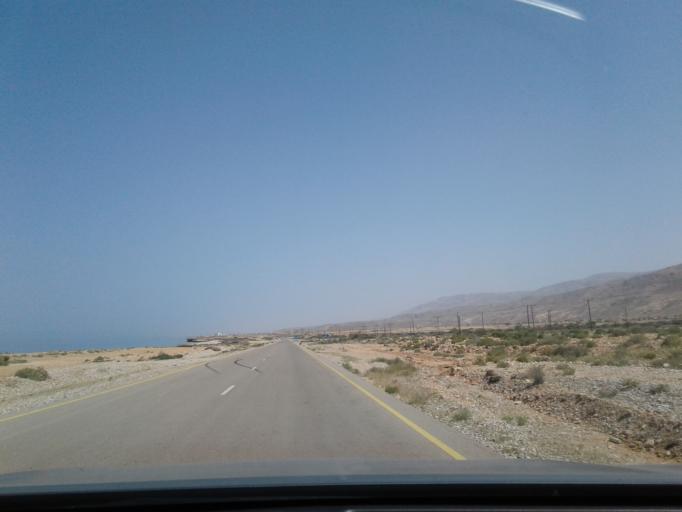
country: OM
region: Ash Sharqiyah
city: Al Qabil
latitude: 23.0375
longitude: 59.0770
